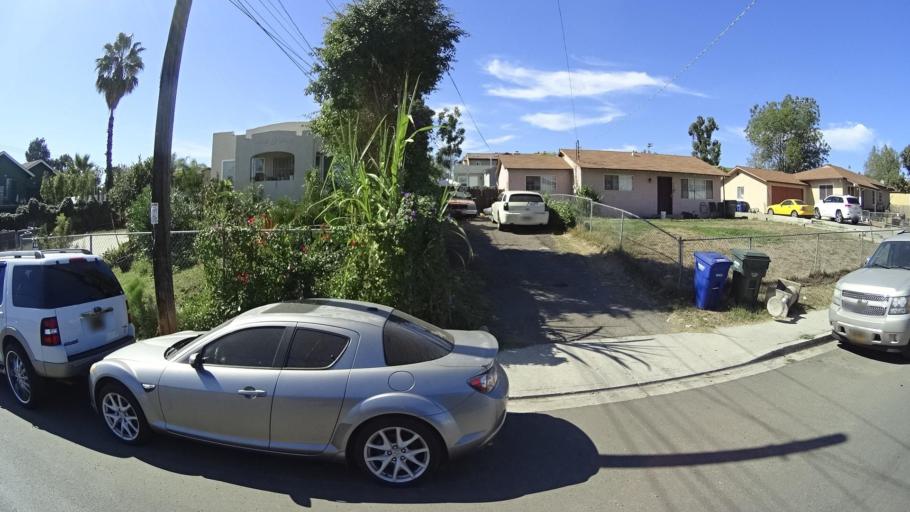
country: US
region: California
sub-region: San Diego County
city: La Presa
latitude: 32.7154
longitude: -117.0056
